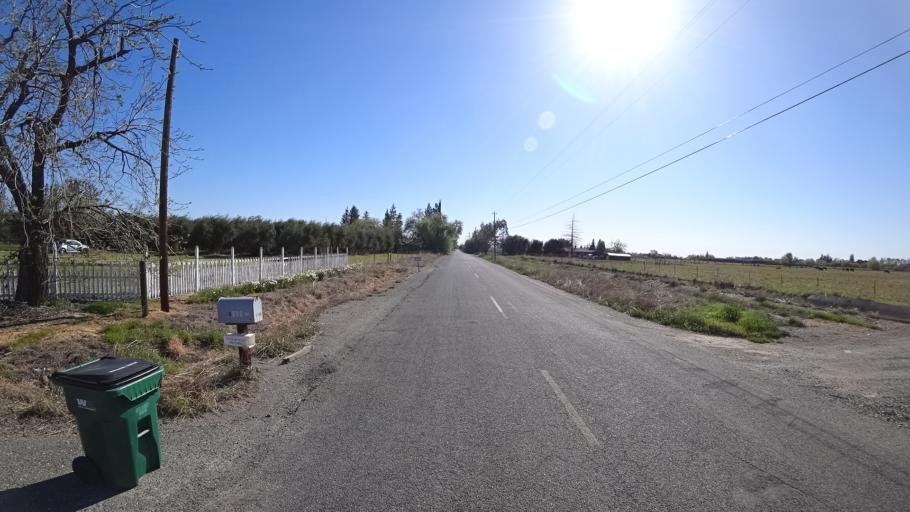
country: US
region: California
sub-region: Glenn County
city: Orland
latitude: 39.7440
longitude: -122.2250
